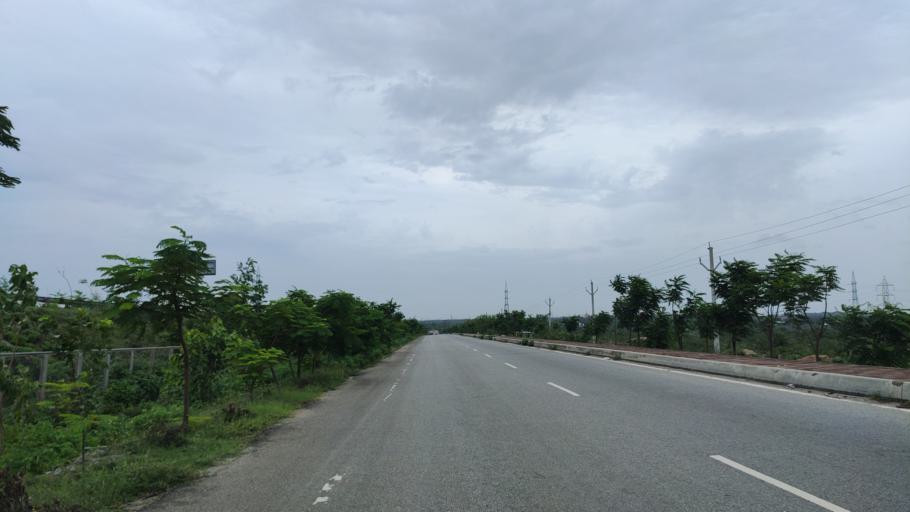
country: IN
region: Telangana
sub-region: Rangareddi
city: Secunderabad
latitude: 17.5792
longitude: 78.5862
